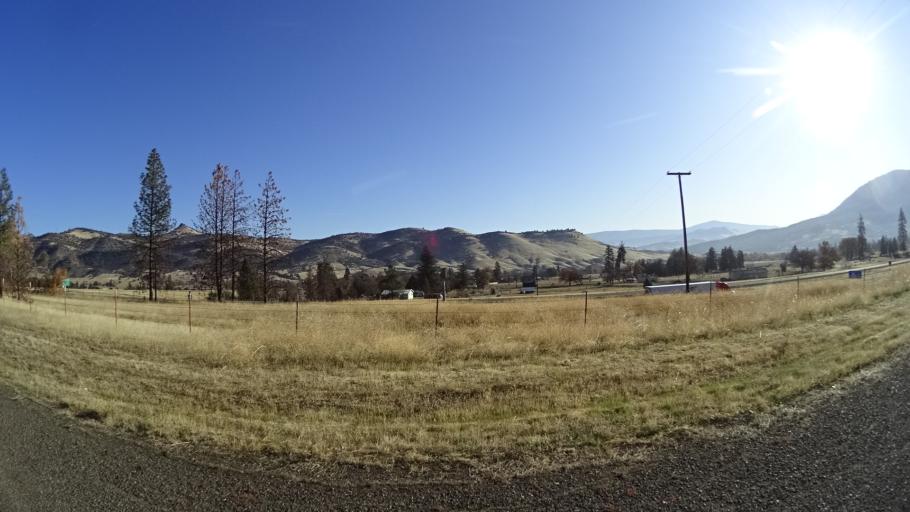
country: US
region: California
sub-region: Siskiyou County
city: Yreka
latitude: 41.9076
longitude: -122.5696
